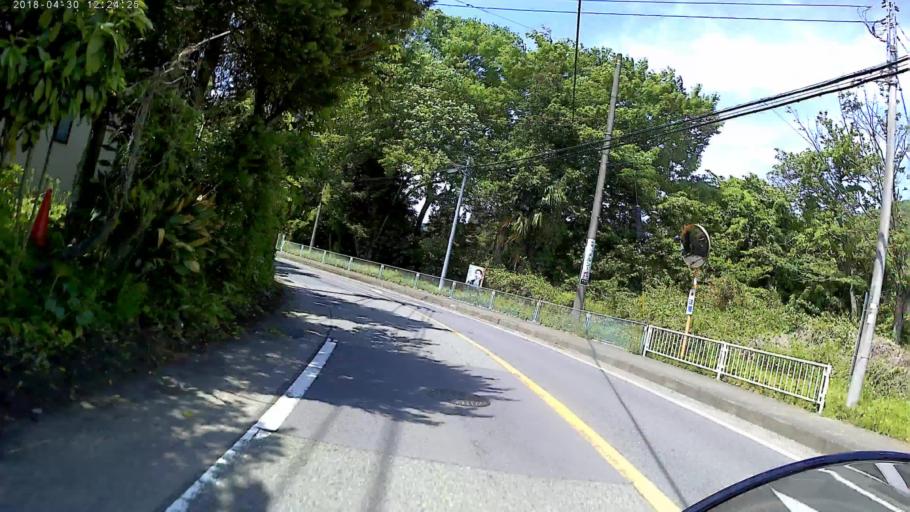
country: JP
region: Tokyo
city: Hachioji
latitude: 35.5769
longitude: 139.2749
